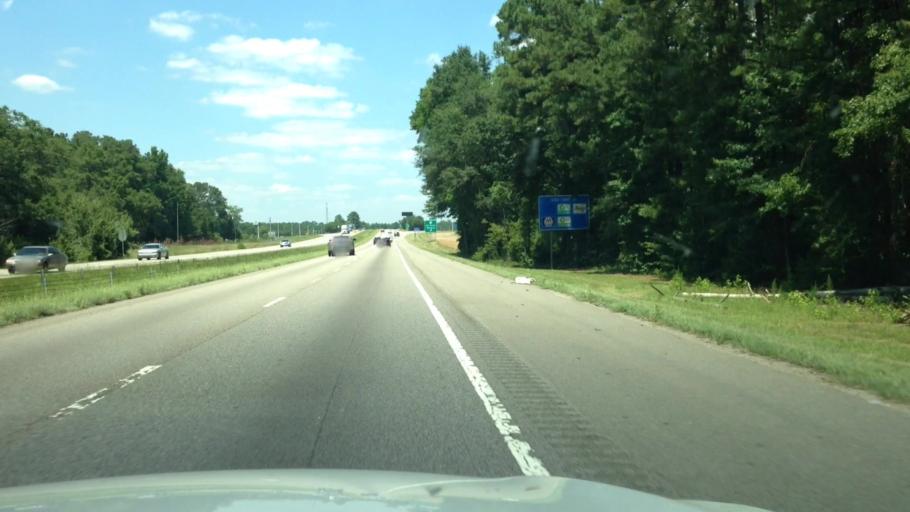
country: US
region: North Carolina
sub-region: Robeson County
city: Saint Pauls
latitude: 34.8044
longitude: -78.9890
